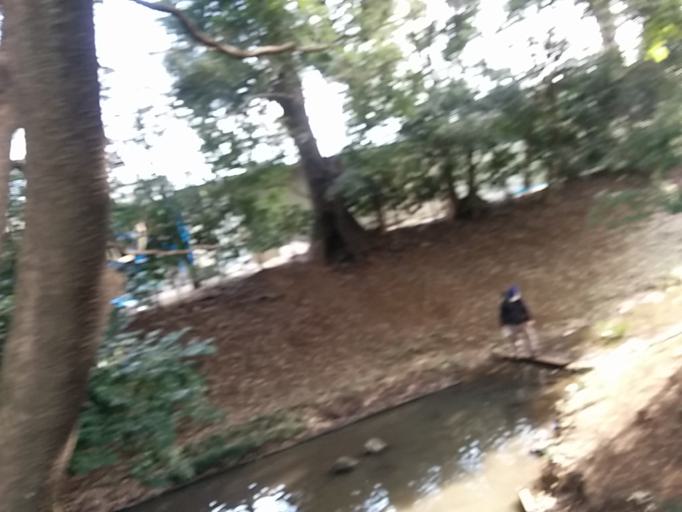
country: JP
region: Saitama
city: Kawagoe
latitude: 35.9170
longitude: 139.4899
